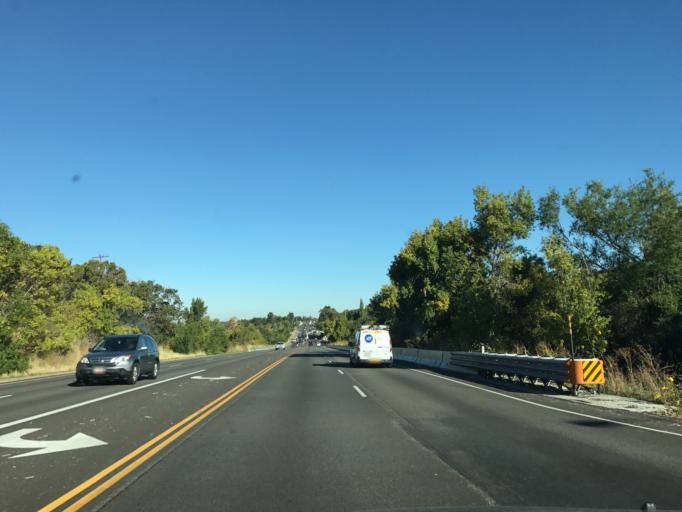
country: US
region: Utah
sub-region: Weber County
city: Uintah
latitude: 41.1651
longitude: -111.9425
